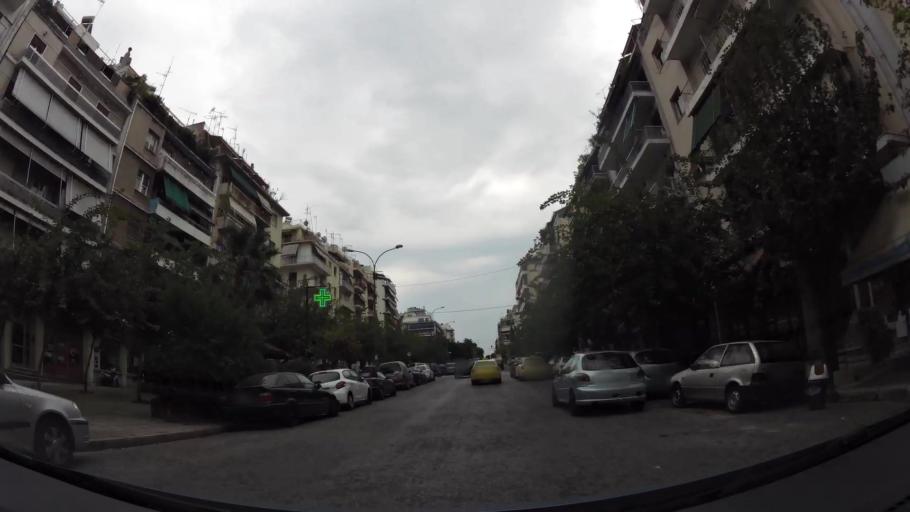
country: GR
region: Attica
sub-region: Nomarchia Athinas
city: Vyronas
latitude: 37.9664
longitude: 23.7480
